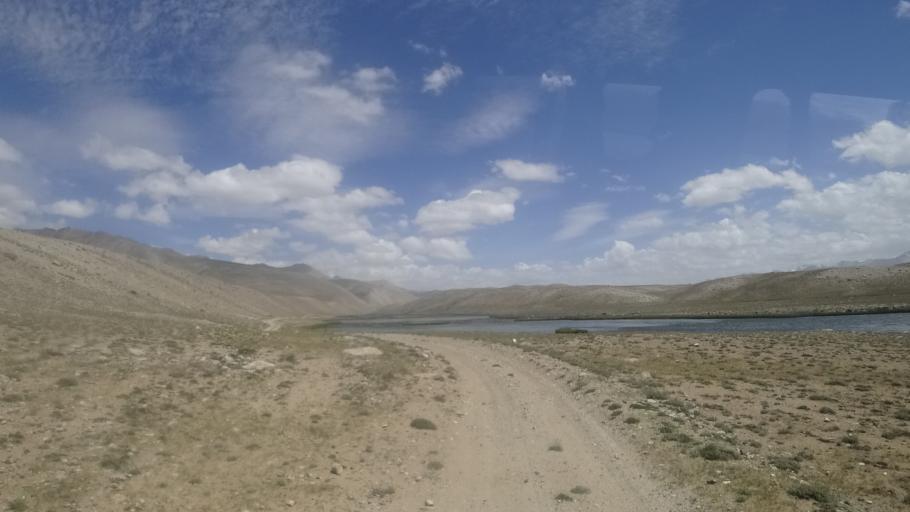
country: TJ
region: Gorno-Badakhshan
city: Murghob
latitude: 37.4689
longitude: 73.4262
